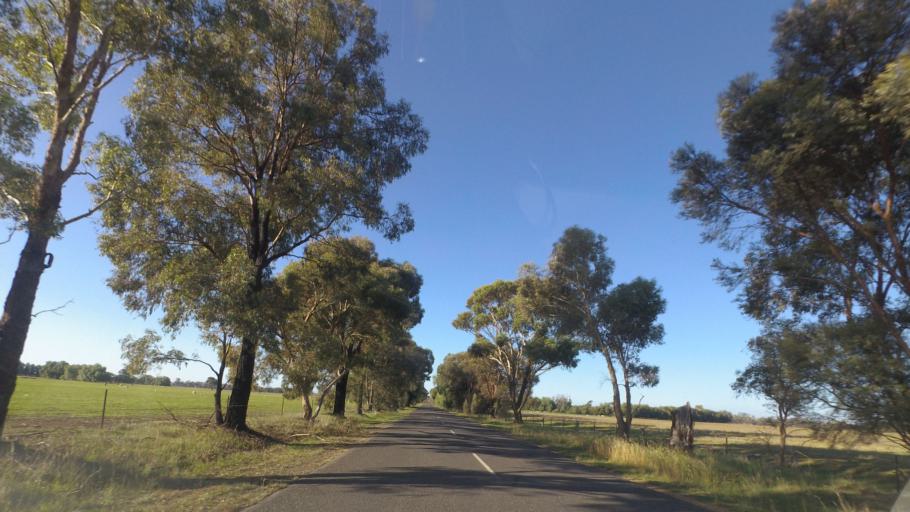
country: AU
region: Victoria
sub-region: Greater Bendigo
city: Epsom
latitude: -36.6482
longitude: 144.5282
